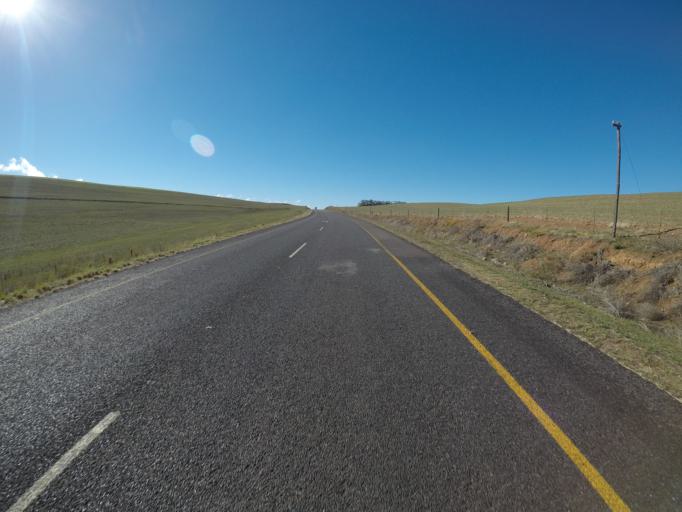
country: ZA
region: Western Cape
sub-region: Overberg District Municipality
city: Caledon
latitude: -34.1443
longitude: 19.4972
